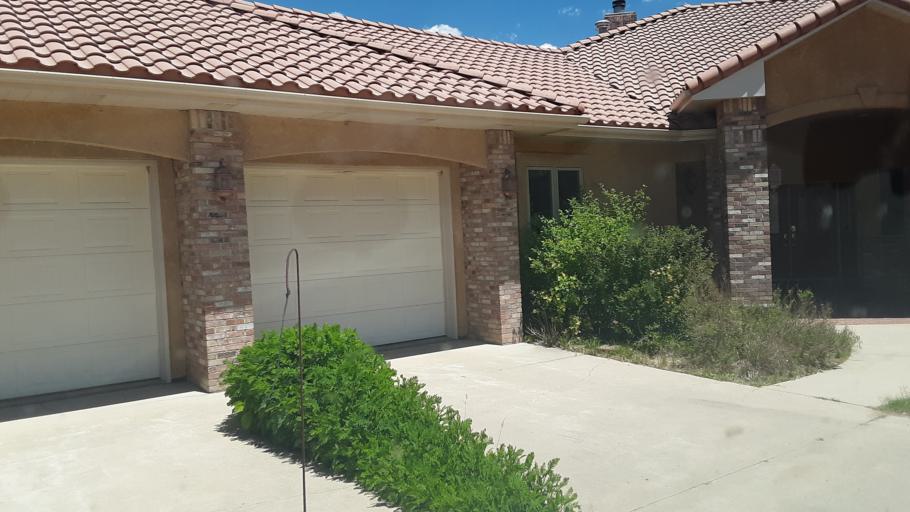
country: US
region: Colorado
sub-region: Custer County
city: Westcliffe
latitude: 38.2812
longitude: -105.6064
